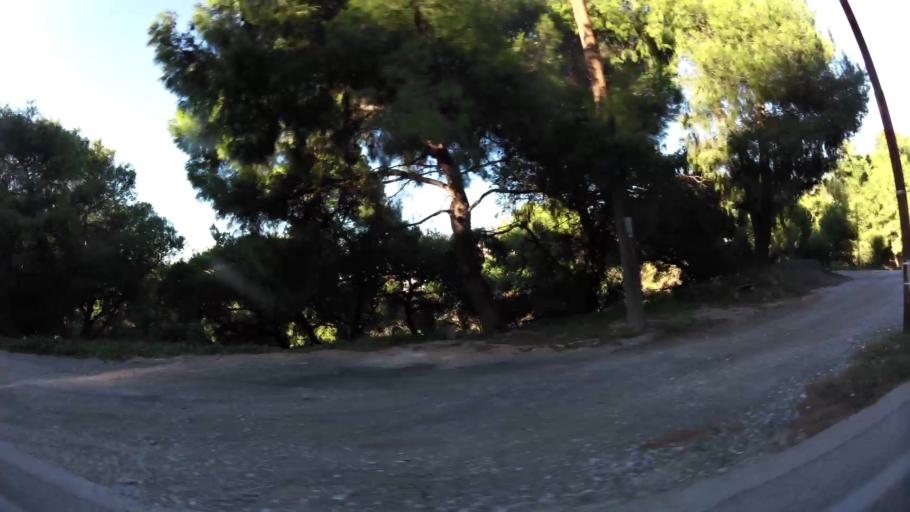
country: GR
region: Attica
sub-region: Nomarchia Athinas
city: Nea Penteli
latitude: 38.0525
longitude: 23.8491
